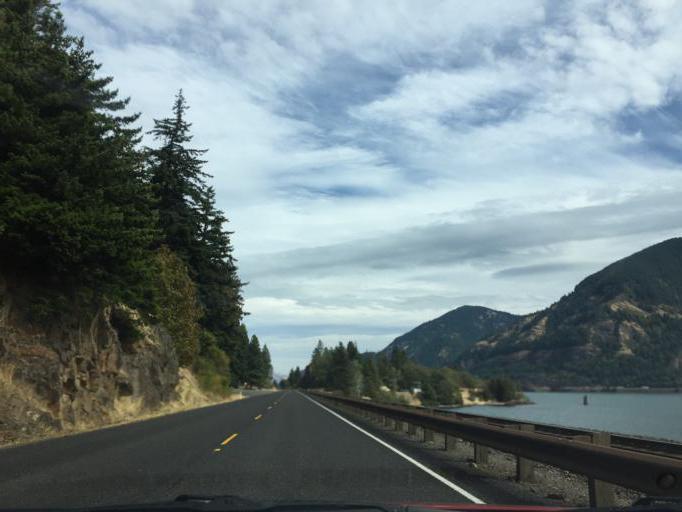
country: US
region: Washington
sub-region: Skamania County
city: Carson
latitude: 45.6989
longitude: -121.7119
